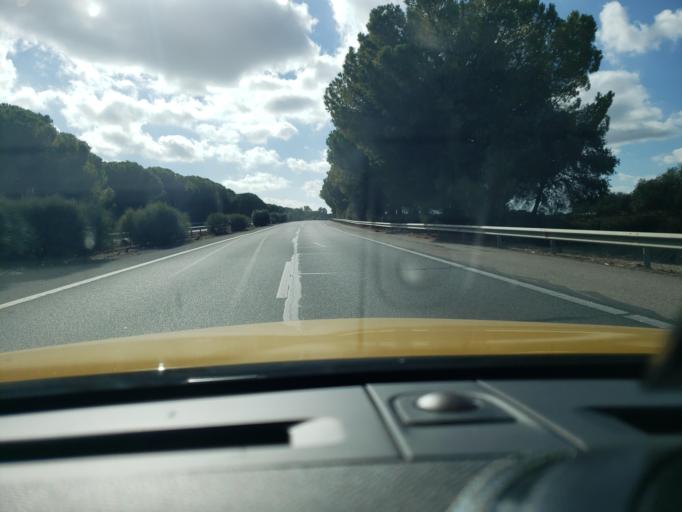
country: ES
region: Andalusia
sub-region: Provincia de Sevilla
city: Lebrija
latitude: 36.8629
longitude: -5.9947
